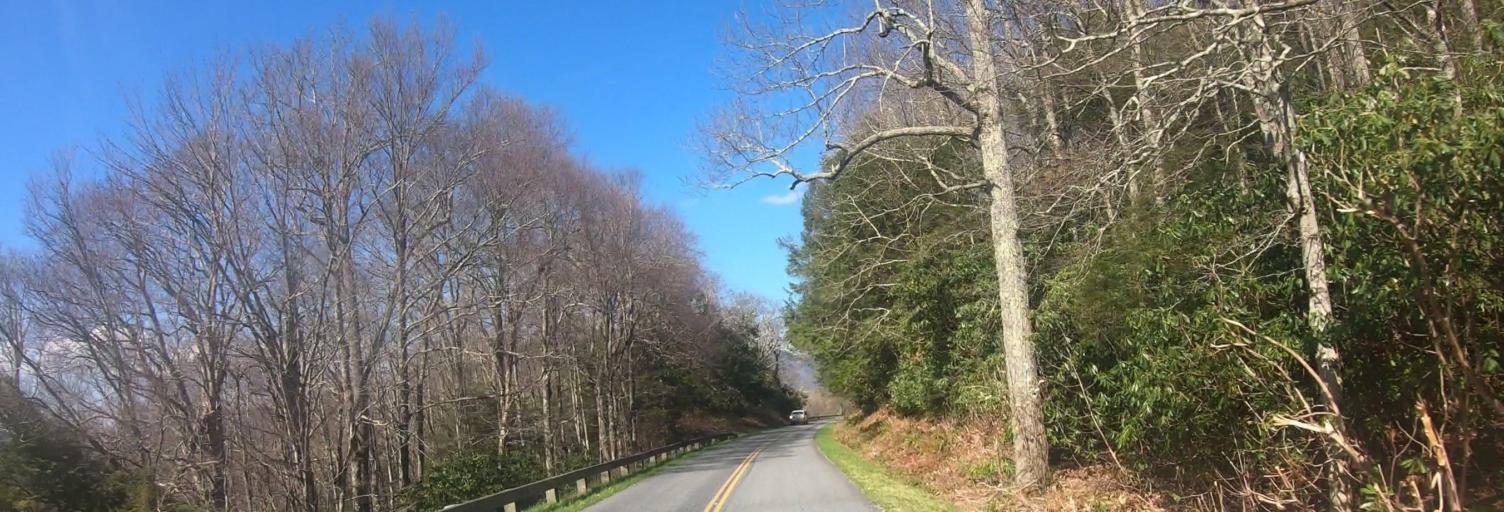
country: US
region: North Carolina
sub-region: Avery County
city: Newland
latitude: 36.0666
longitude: -81.8452
